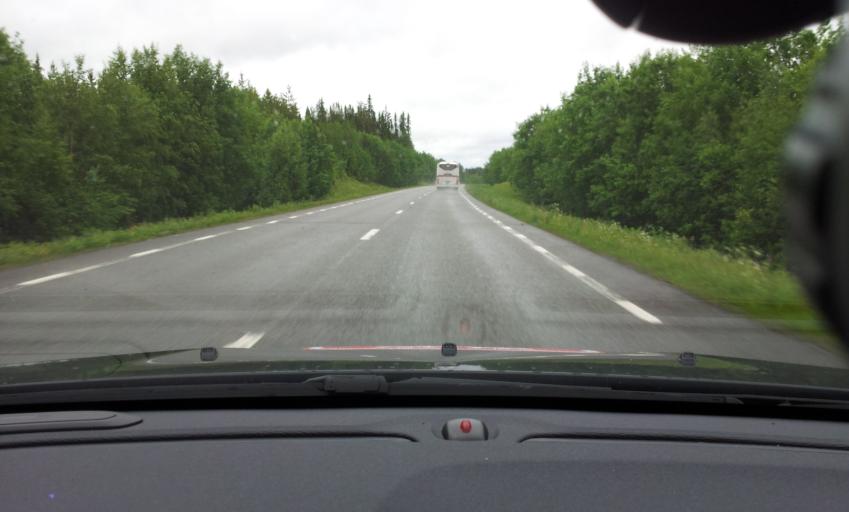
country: SE
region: Jaemtland
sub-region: Krokoms Kommun
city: Krokom
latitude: 63.5630
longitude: 14.6101
